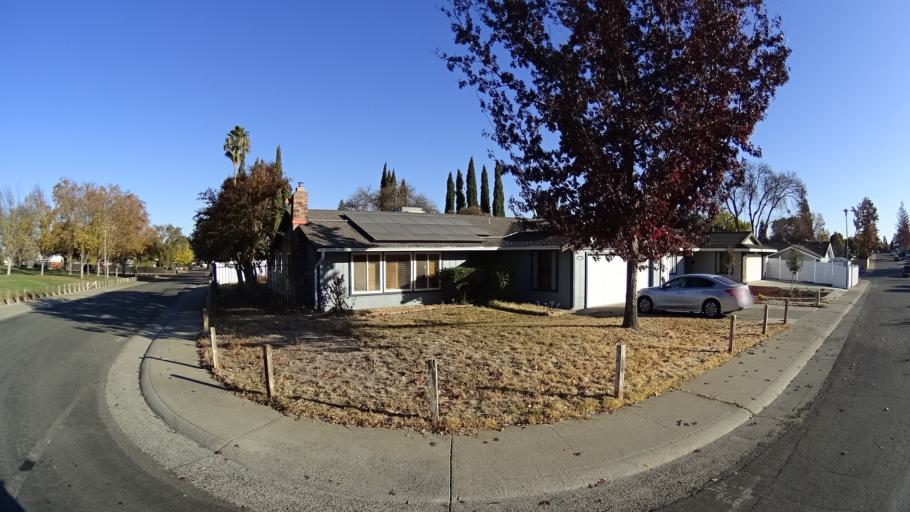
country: US
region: California
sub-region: Sacramento County
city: Fair Oaks
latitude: 38.6719
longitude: -121.3035
